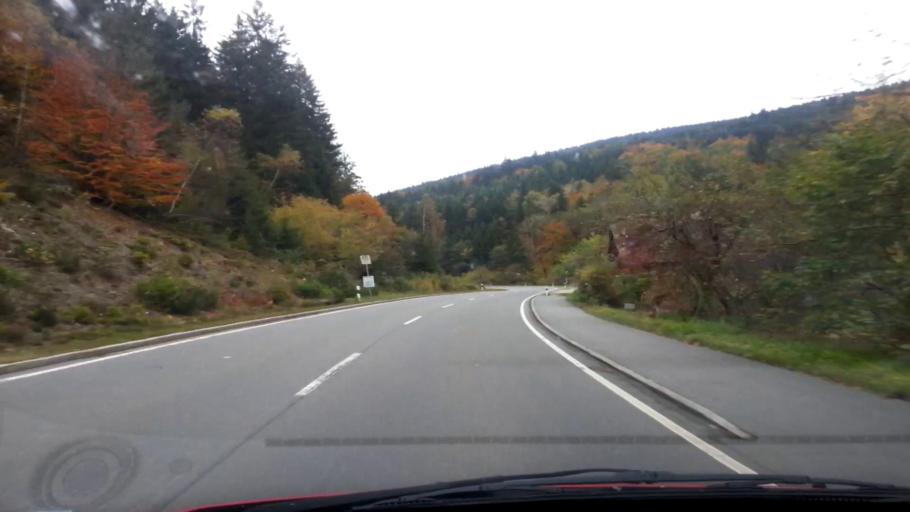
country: DE
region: Bavaria
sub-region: Upper Franconia
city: Warmensteinach
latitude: 49.9635
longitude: 11.7625
